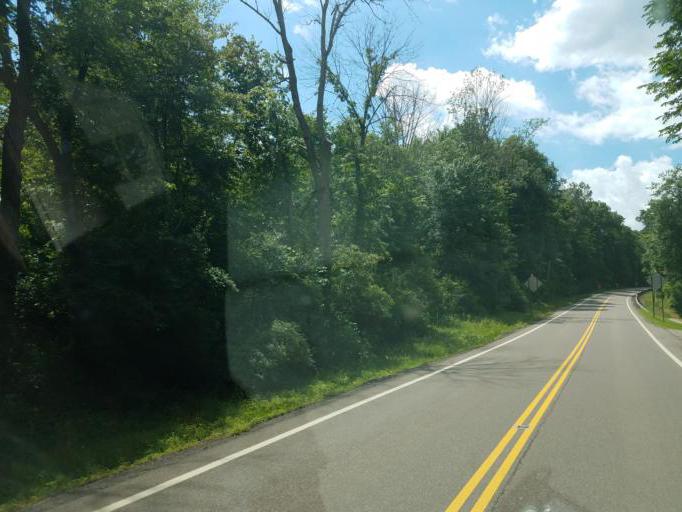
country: US
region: Ohio
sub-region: Knox County
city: Oak Hill
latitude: 40.3921
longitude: -82.2781
